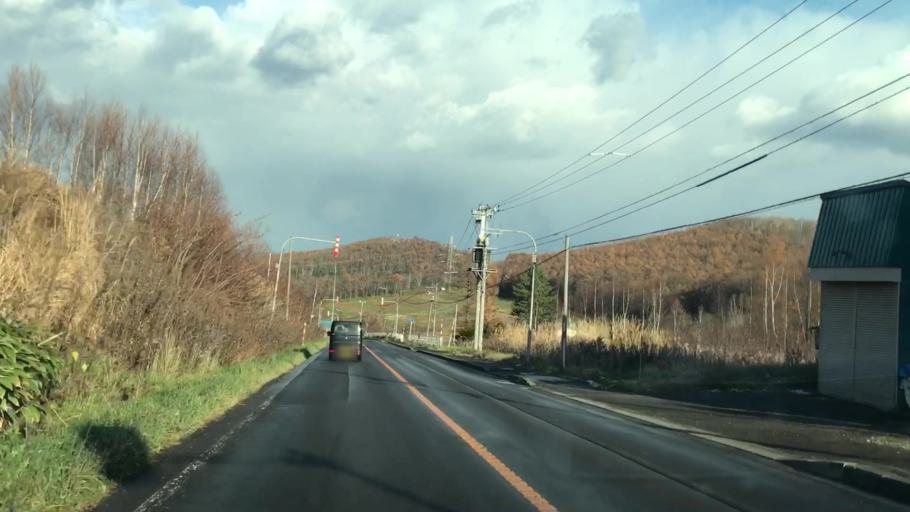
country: JP
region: Hokkaido
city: Otaru
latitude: 43.1906
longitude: 140.9586
